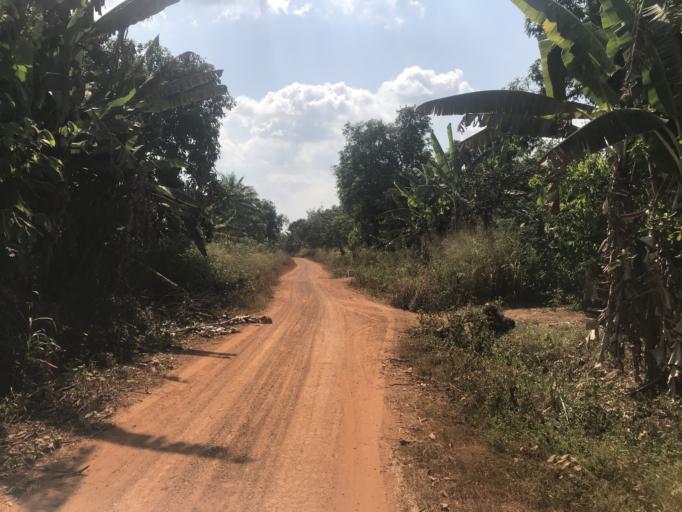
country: NG
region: Osun
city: Ibokun
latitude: 7.8060
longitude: 4.6898
